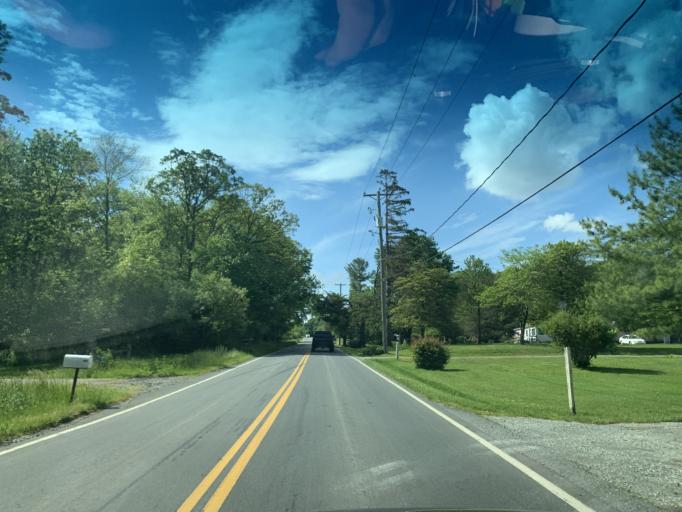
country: US
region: Maryland
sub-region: Cecil County
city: Rising Sun
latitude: 39.7099
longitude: -76.1489
